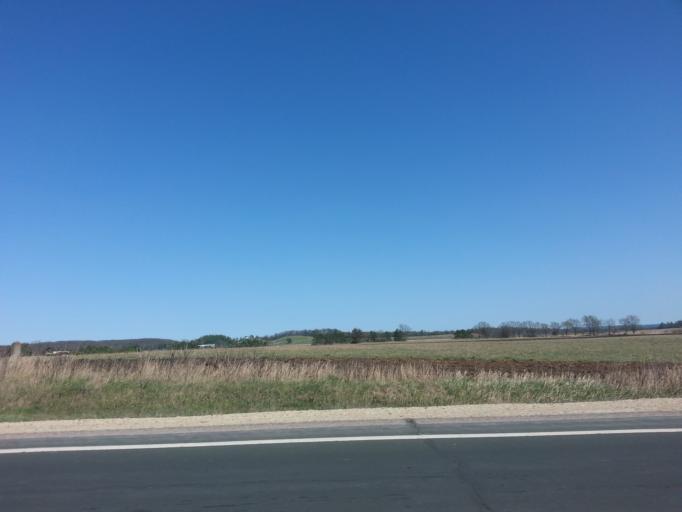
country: US
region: Wisconsin
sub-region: Pepin County
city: Durand
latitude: 44.7182
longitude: -91.9331
